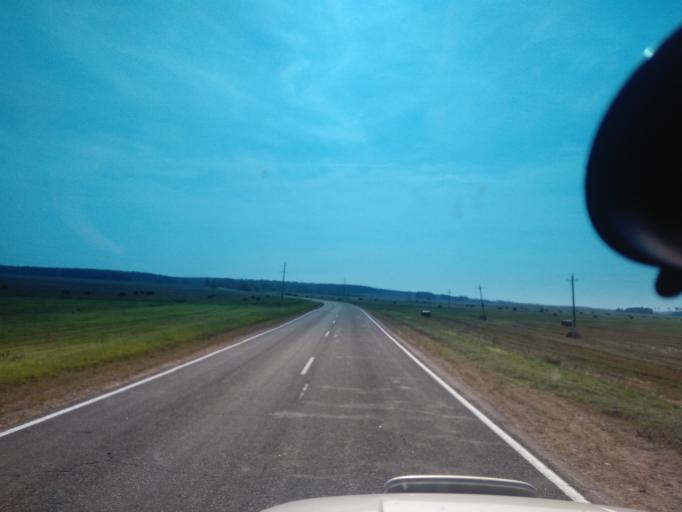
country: BY
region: Minsk
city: Uzda
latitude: 53.3971
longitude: 27.2308
